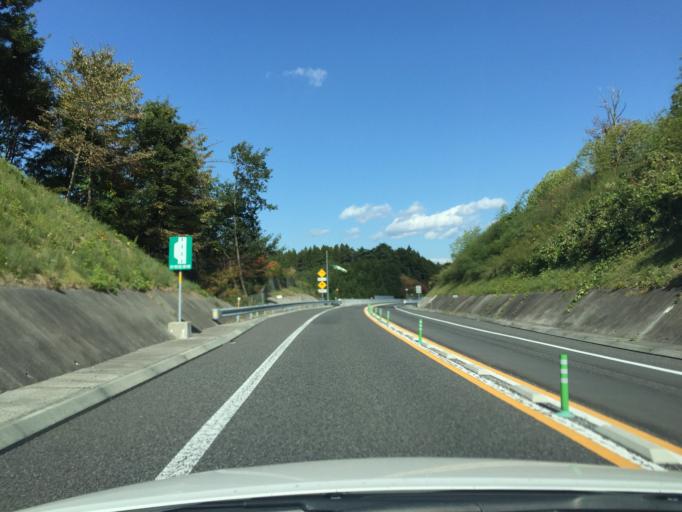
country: JP
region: Fukushima
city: Ishikawa
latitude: 37.2244
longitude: 140.5452
